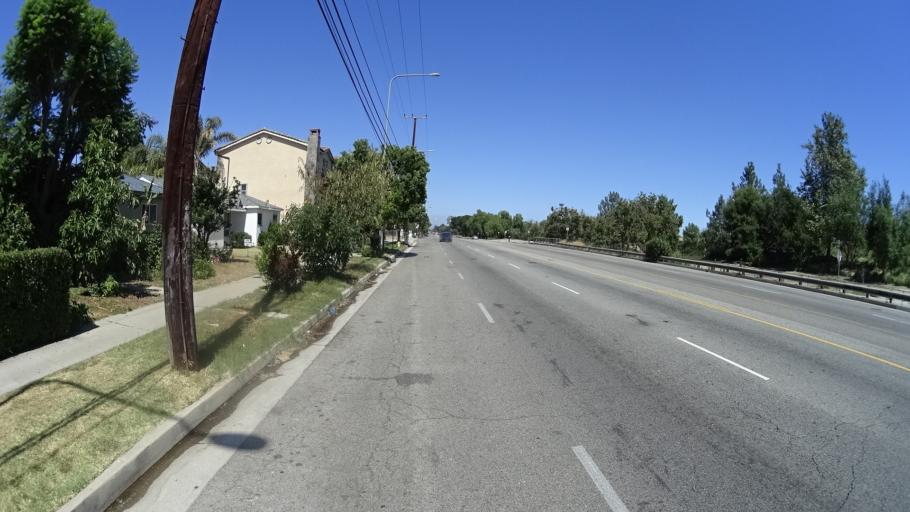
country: US
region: California
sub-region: Los Angeles County
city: Van Nuys
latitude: 34.1867
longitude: -118.4987
